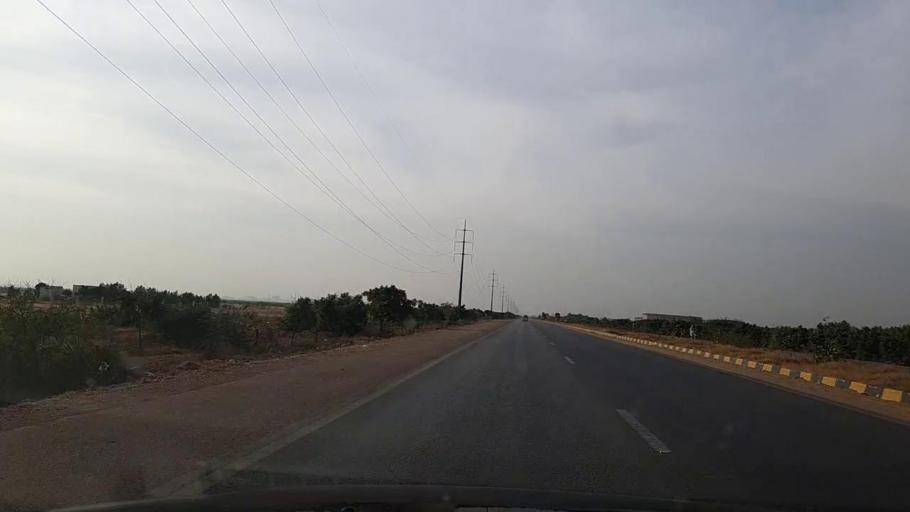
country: PK
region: Sindh
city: Gharo
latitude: 24.8247
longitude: 67.4758
